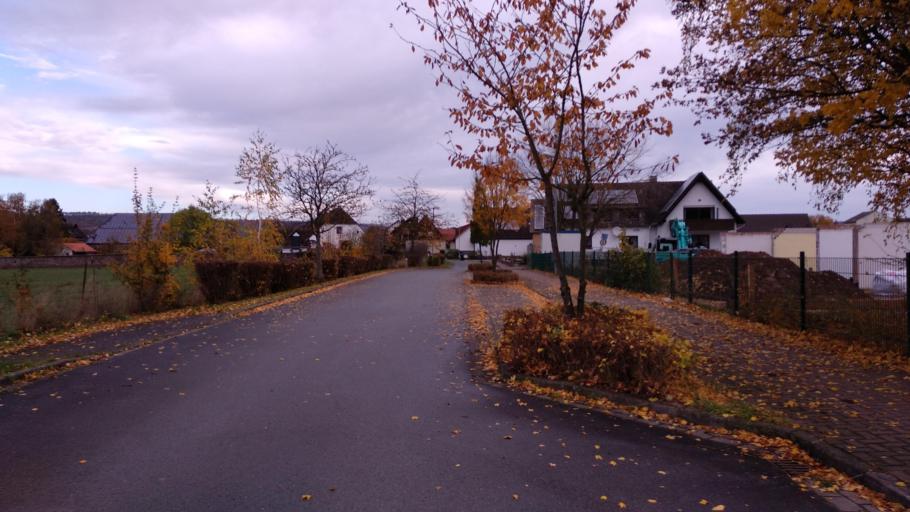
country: DE
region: North Rhine-Westphalia
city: Beverungen
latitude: 51.6581
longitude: 9.3830
